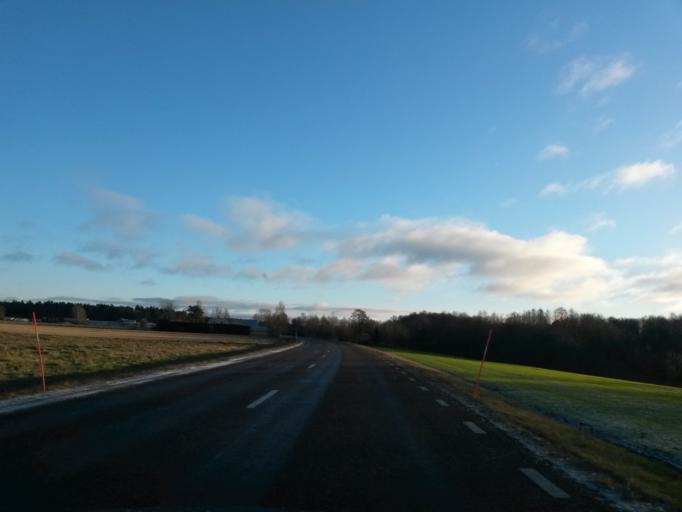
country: SE
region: Vaestra Goetaland
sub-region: Essunga Kommun
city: Nossebro
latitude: 58.2384
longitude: 12.7108
